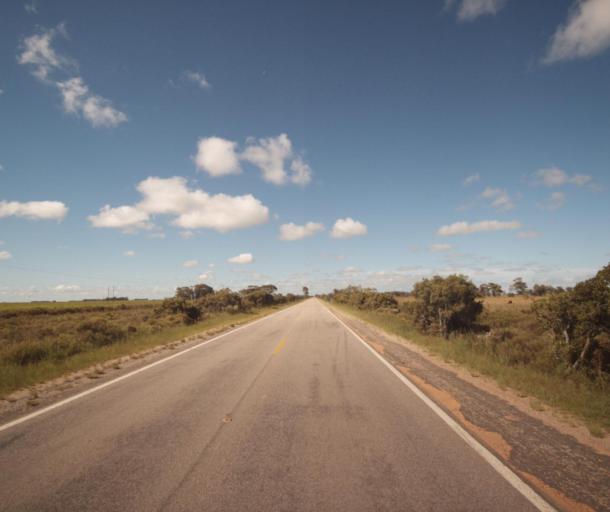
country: BR
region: Rio Grande do Sul
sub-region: Santa Vitoria Do Palmar
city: Santa Vitoria do Palmar
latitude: -33.3842
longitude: -53.2014
